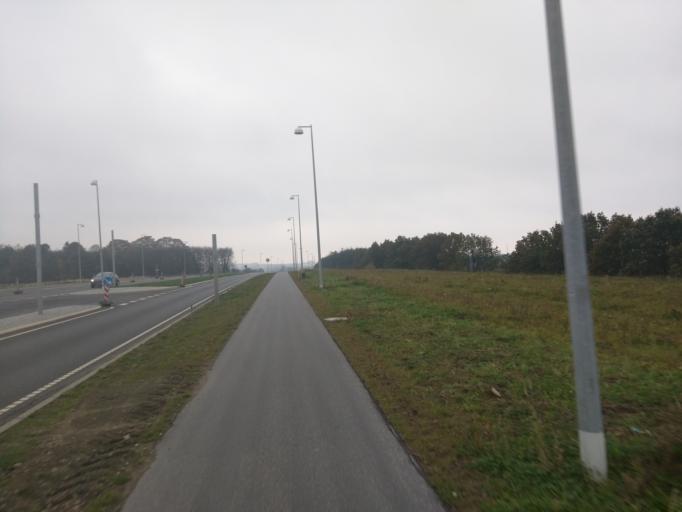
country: DK
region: Central Jutland
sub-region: Silkeborg Kommune
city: Silkeborg
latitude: 56.2027
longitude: 9.5132
